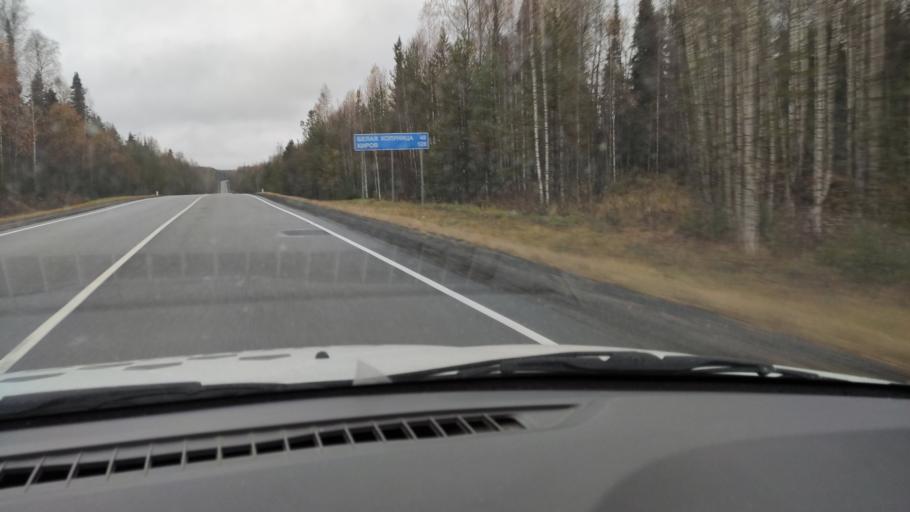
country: RU
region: Kirov
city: Chernaya Kholunitsa
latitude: 58.8628
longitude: 51.5974
